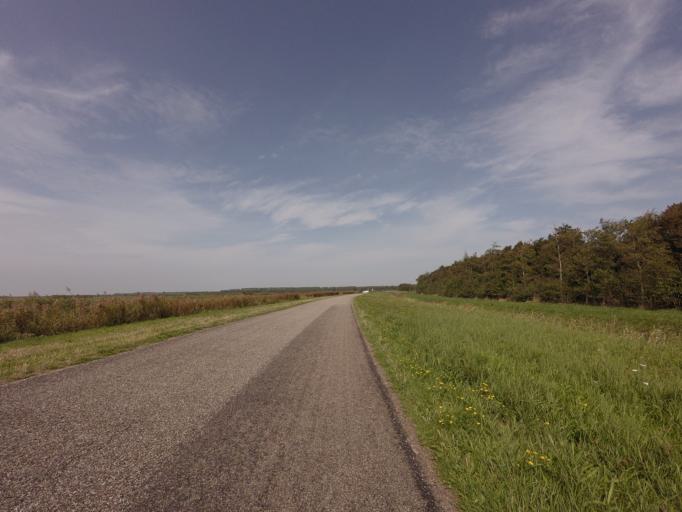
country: NL
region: Groningen
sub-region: Gemeente De Marne
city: Ulrum
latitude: 53.3586
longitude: 6.2613
